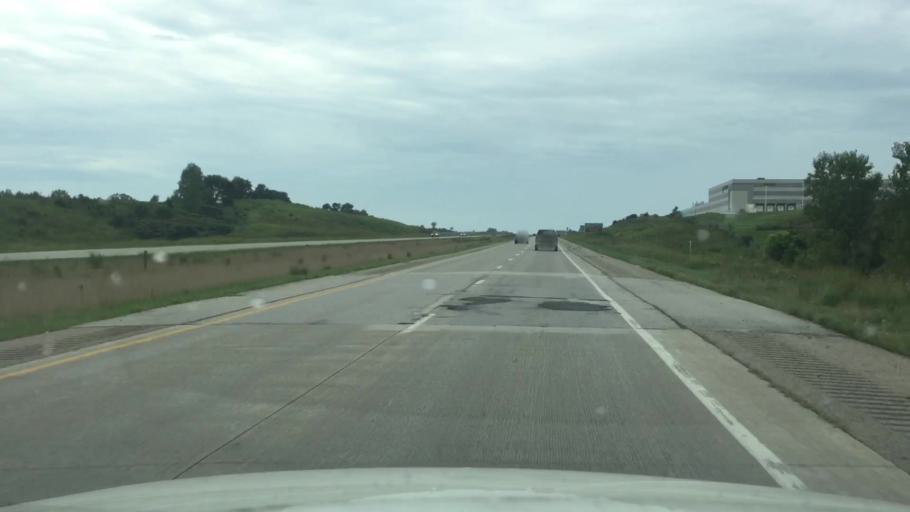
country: US
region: Iowa
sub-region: Warren County
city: Norwalk
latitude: 41.5145
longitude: -93.6669
